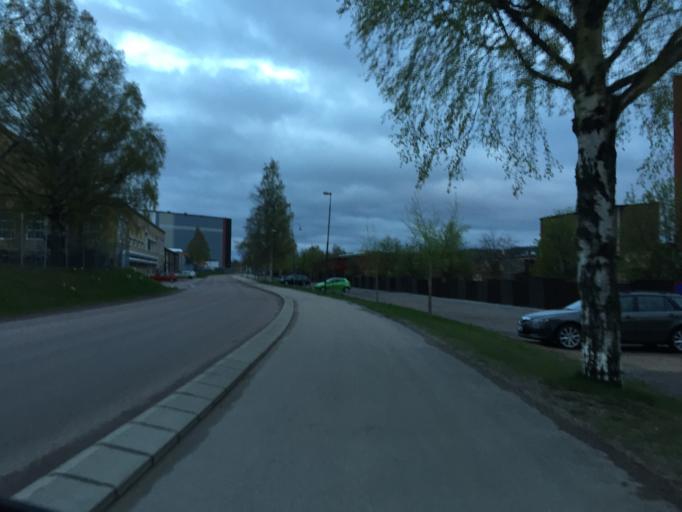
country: SE
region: Dalarna
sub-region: Ludvika Kommun
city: Ludvika
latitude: 60.1425
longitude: 15.1712
